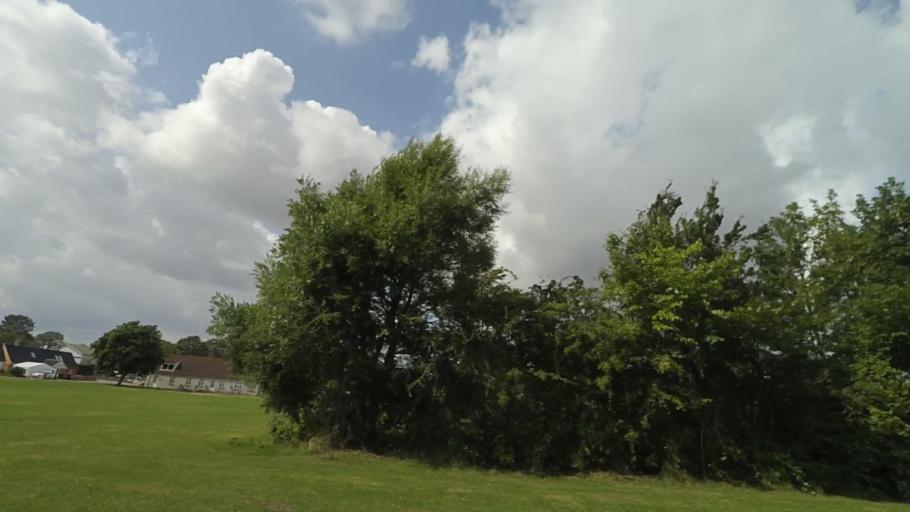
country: DK
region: Central Jutland
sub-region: Norddjurs Kommune
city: Allingabro
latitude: 56.5387
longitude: 10.3652
